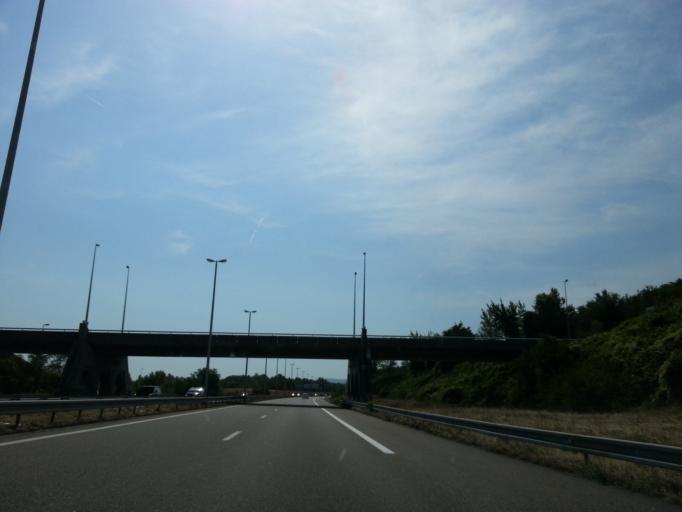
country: FR
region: Alsace
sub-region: Departement du Haut-Rhin
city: Hesingue
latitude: 47.6019
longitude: 7.5348
